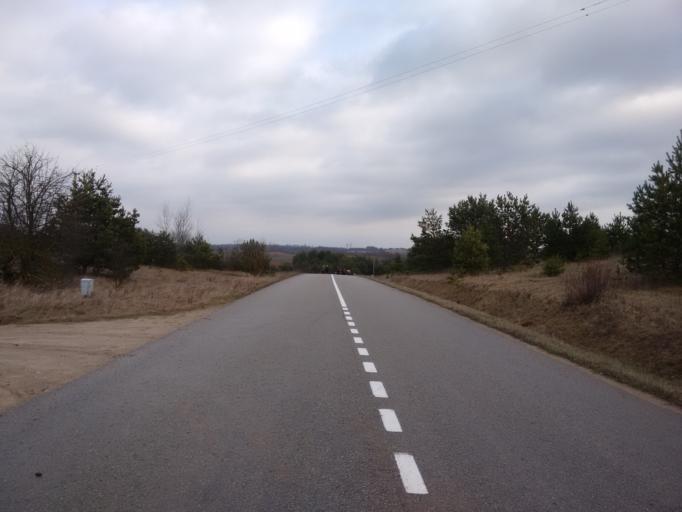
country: LT
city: Veisiejai
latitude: 54.2428
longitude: 23.8487
